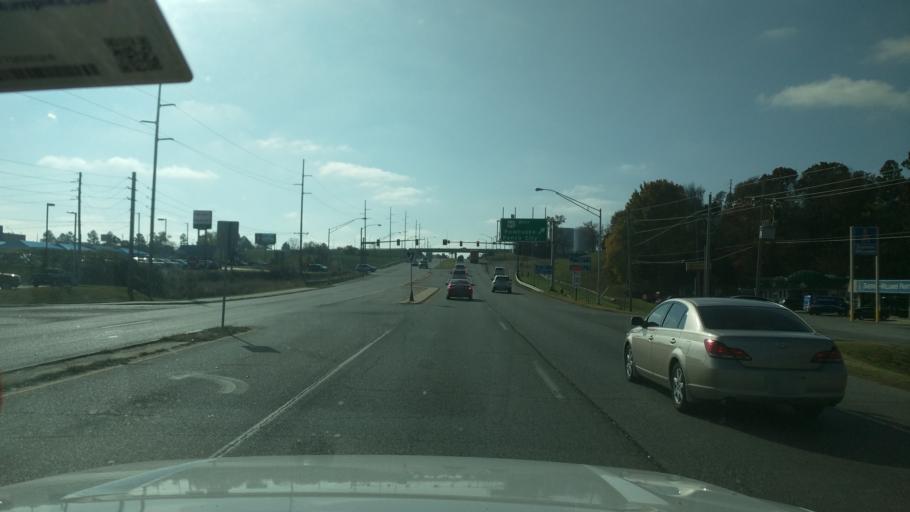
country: US
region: Oklahoma
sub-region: Washington County
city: Bartlesville
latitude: 36.7470
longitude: -95.9355
